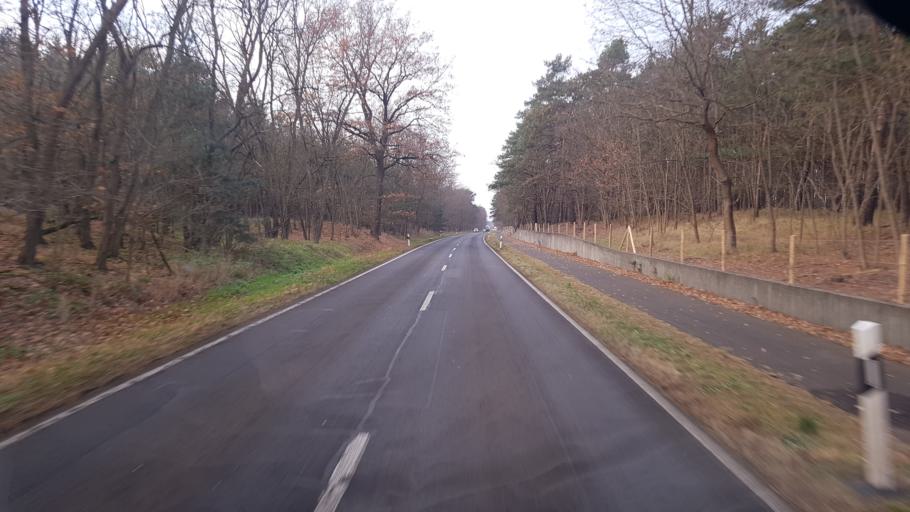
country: DE
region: Brandenburg
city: Ziltendorf
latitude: 52.1948
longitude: 14.6417
